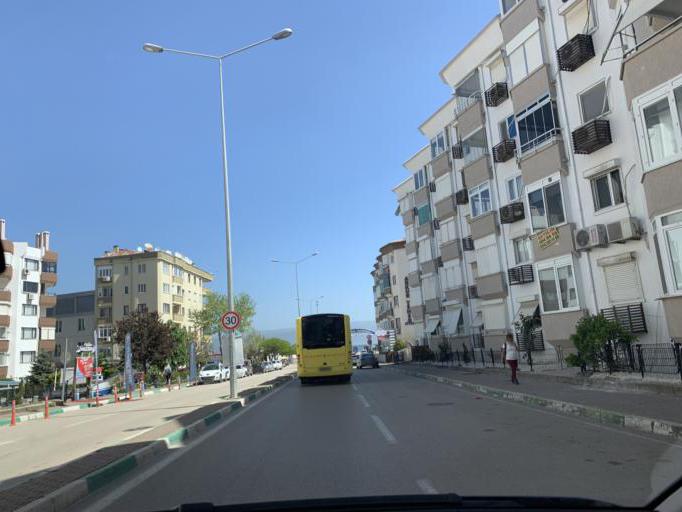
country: TR
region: Bursa
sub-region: Mudanya
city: Mudanya
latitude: 40.3546
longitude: 28.9260
